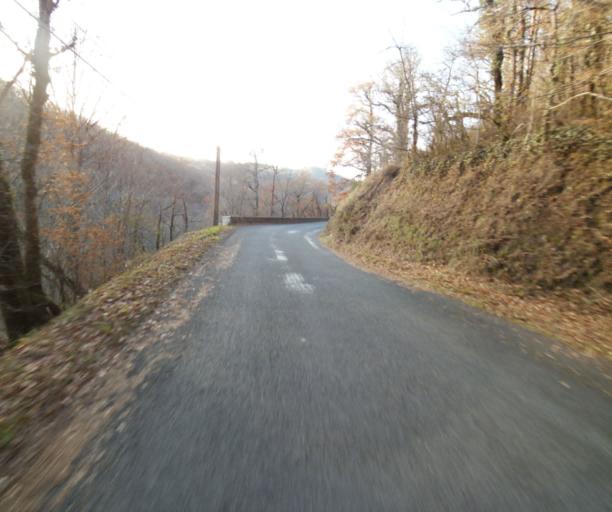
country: FR
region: Limousin
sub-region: Departement de la Correze
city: Laguenne
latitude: 45.2404
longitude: 1.7963
